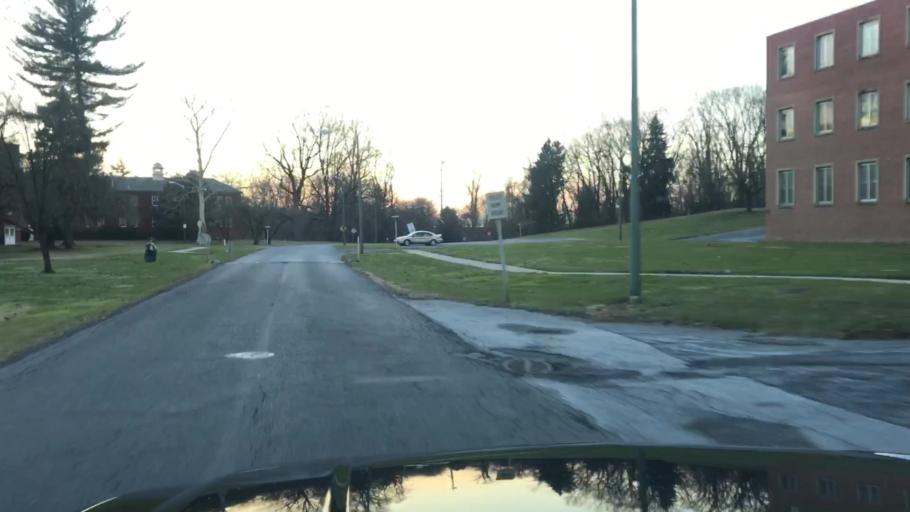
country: US
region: Pennsylvania
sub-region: Dauphin County
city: Harrisburg
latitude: 40.2867
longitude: -76.8726
